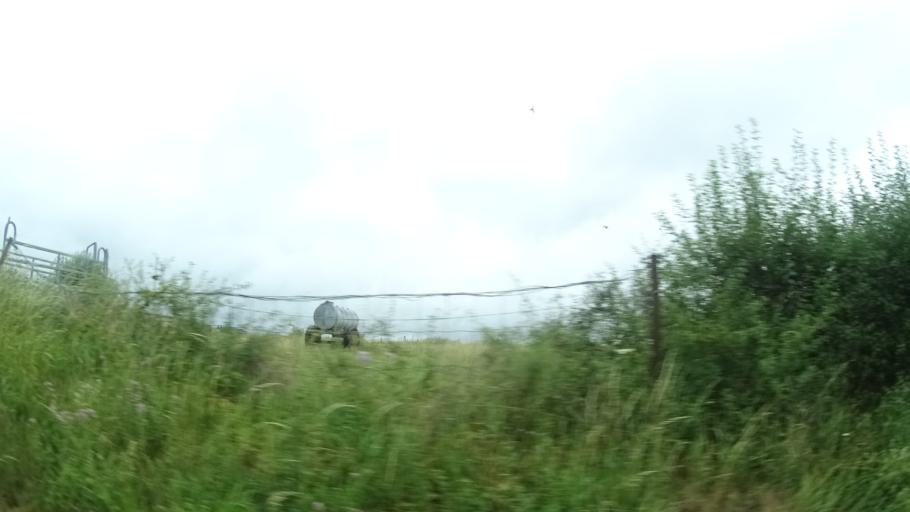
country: LU
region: Luxembourg
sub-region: Canton de Capellen
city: Clemency
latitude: 49.5959
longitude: 5.8626
